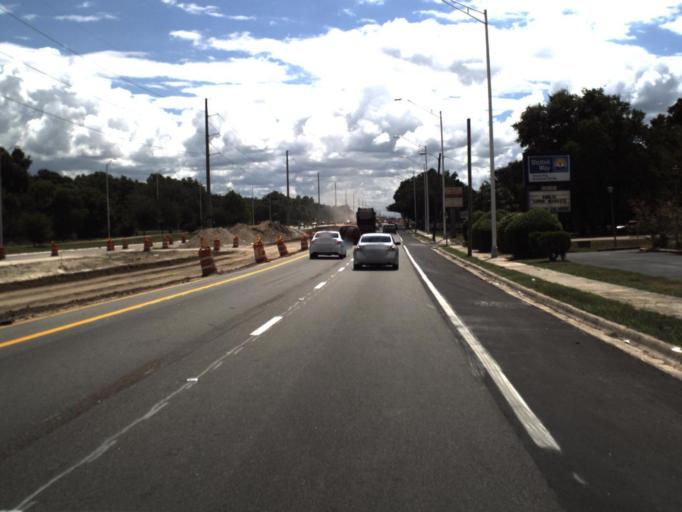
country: US
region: Florida
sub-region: Polk County
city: Highland City
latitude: 27.9630
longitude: -81.8766
